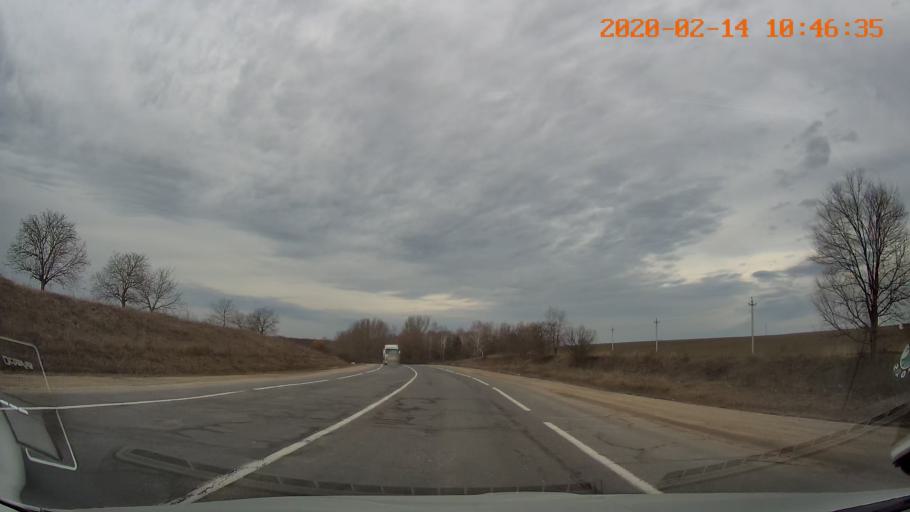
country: MD
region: Riscani
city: Riscani
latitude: 48.0393
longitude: 27.5292
